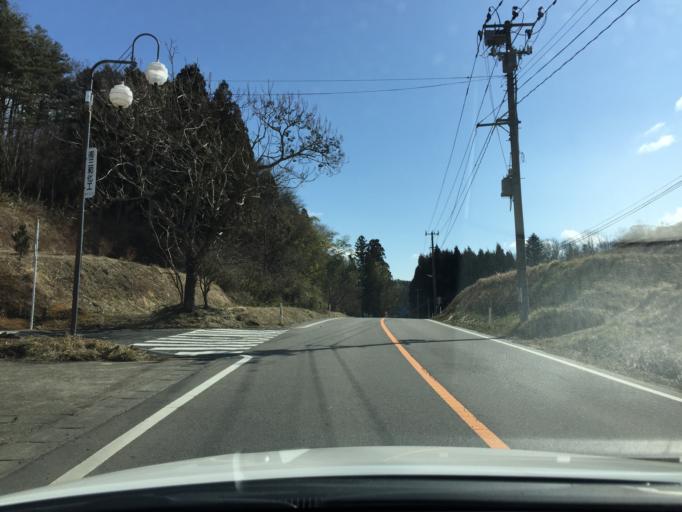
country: JP
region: Fukushima
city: Funehikimachi-funehiki
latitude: 37.3855
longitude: 140.5884
